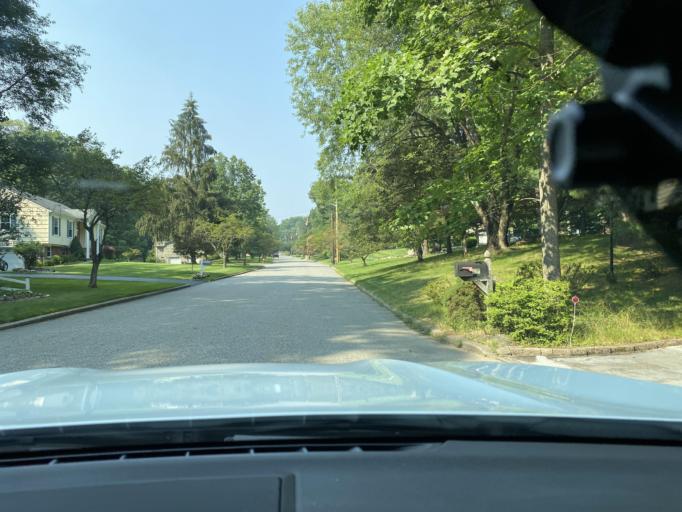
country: US
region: New Jersey
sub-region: Bergen County
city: Mahwah
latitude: 41.0782
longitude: -74.1233
